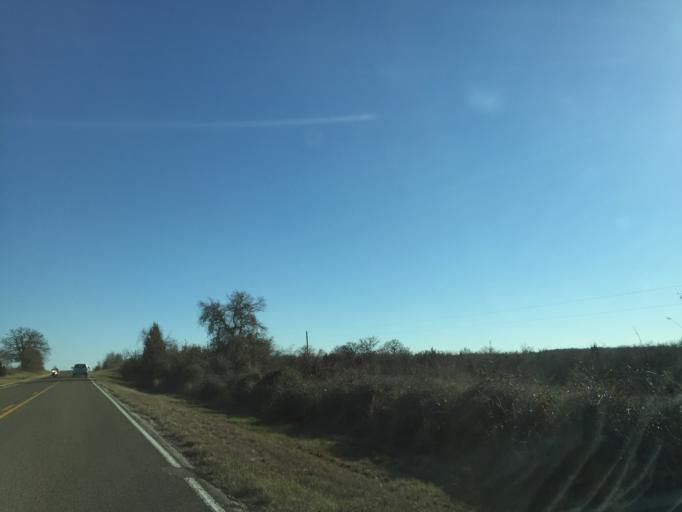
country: US
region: Texas
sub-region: Bastrop County
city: Elgin
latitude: 30.4160
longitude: -97.2560
